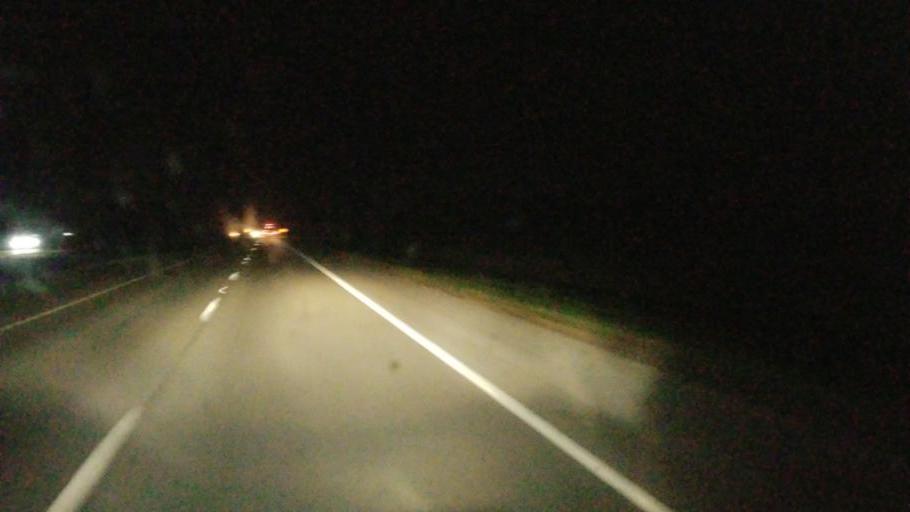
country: US
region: Ohio
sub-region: Allen County
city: Delphos
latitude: 40.8735
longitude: -84.4009
